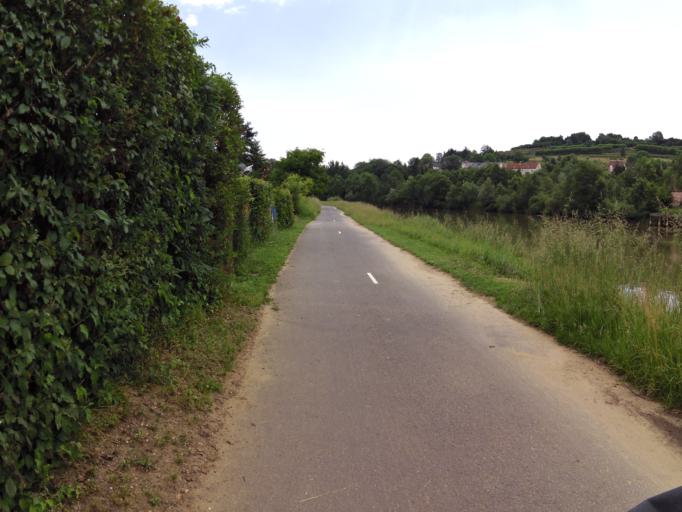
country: FR
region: Champagne-Ardenne
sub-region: Departement des Ardennes
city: Montcy-Notre-Dame
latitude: 49.7725
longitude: 4.7420
